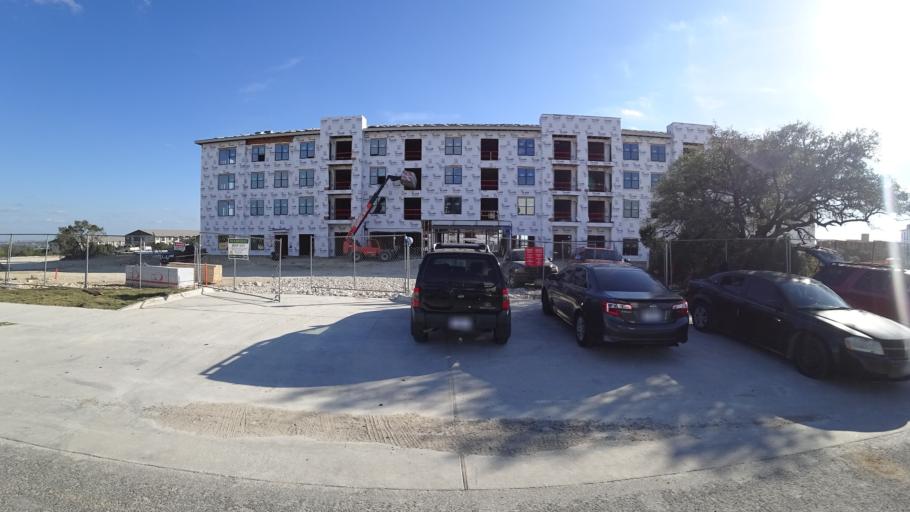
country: US
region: Texas
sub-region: Travis County
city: Barton Creek
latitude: 30.2487
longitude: -97.8604
